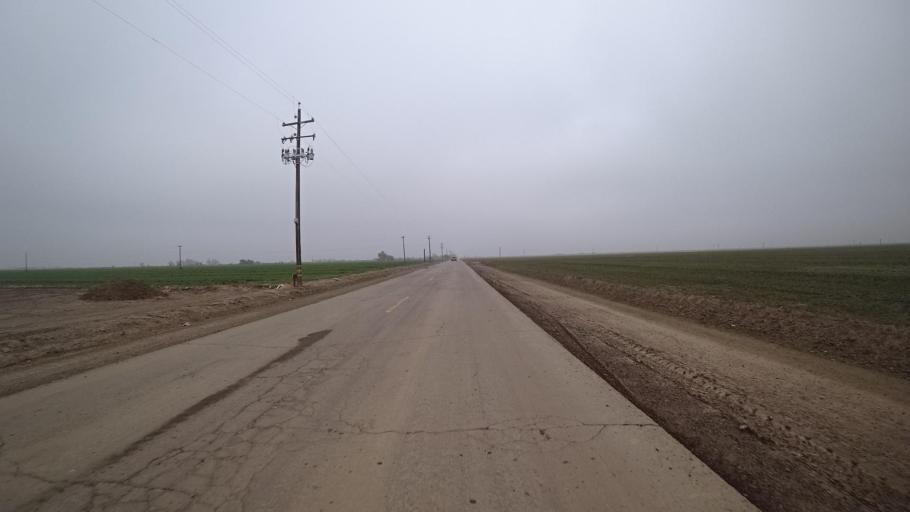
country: US
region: California
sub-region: Kern County
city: Wasco
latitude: 35.6692
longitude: -119.5086
